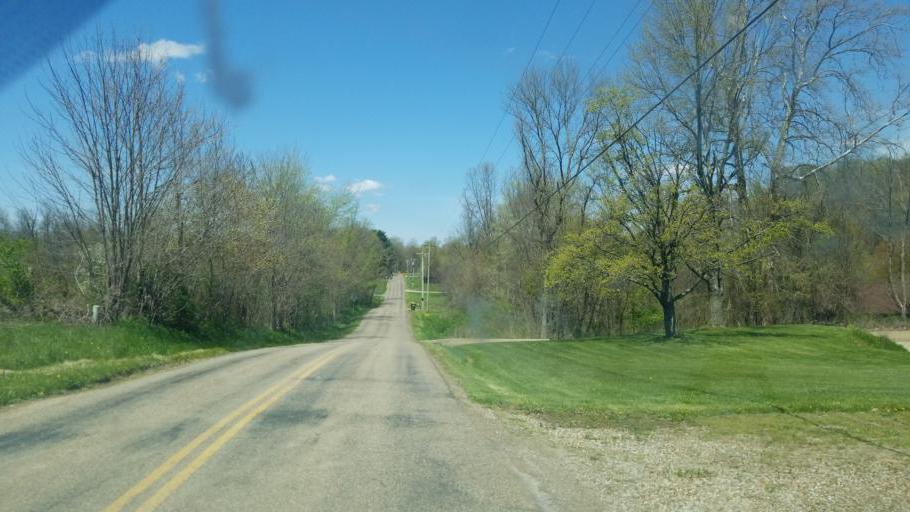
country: US
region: Ohio
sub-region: Richland County
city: Lincoln Heights
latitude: 40.7515
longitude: -82.3974
